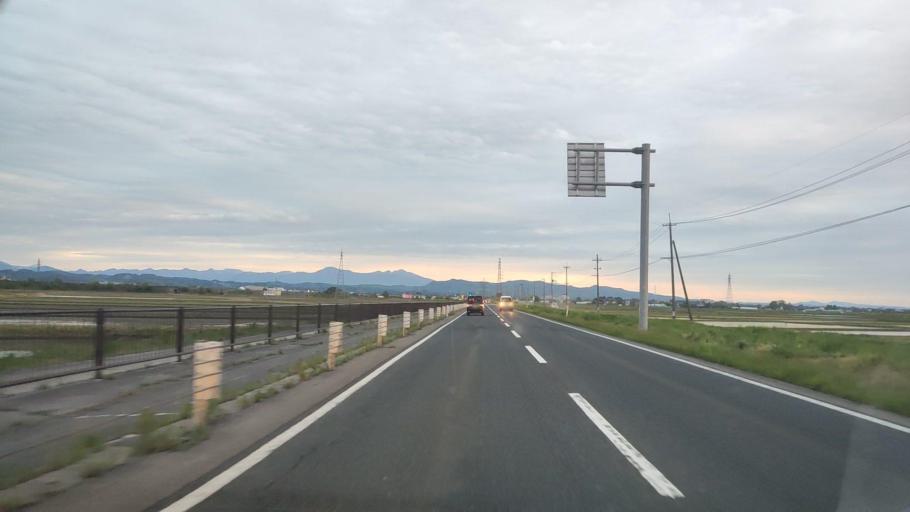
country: JP
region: Niigata
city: Niitsu-honcho
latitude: 37.8099
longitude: 139.1011
